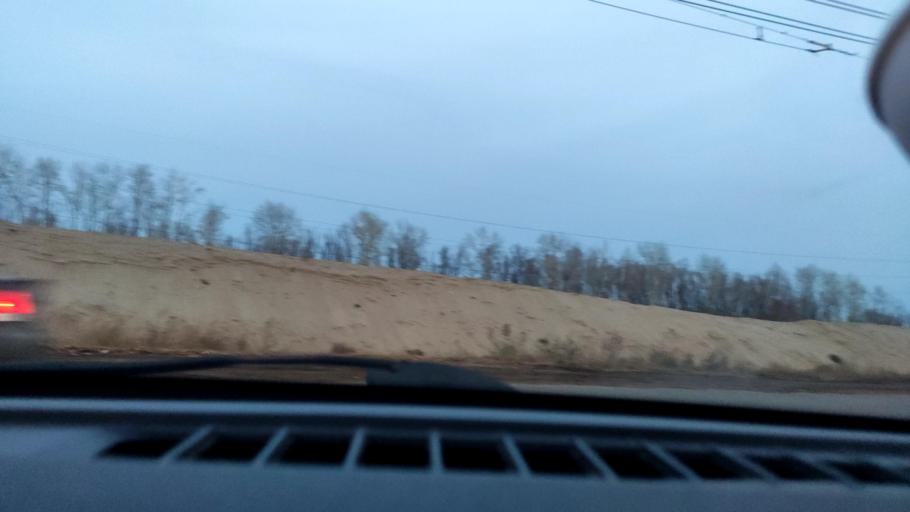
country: RU
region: Samara
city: Samara
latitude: 53.1435
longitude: 50.0977
